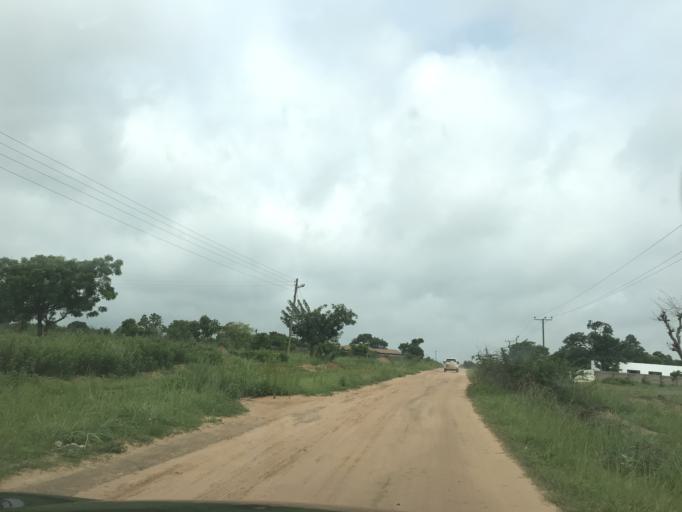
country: GH
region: Upper West
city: Wa
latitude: 10.0280
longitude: -2.4862
